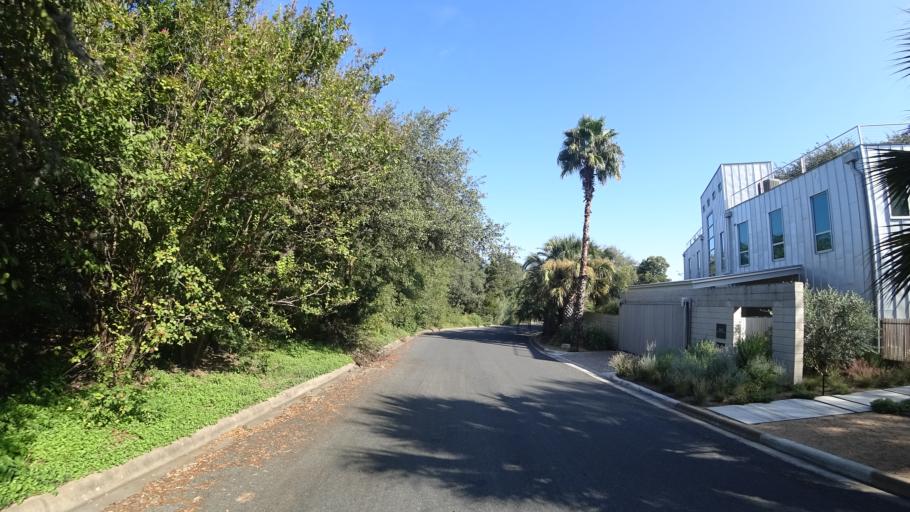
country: US
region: Texas
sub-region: Travis County
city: Austin
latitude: 30.2521
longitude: -97.7451
